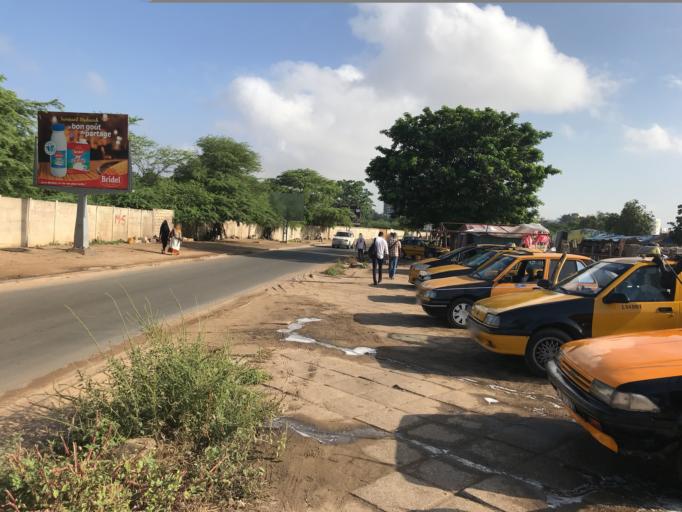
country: SN
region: Dakar
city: Dakar
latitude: 14.6858
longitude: -17.4608
